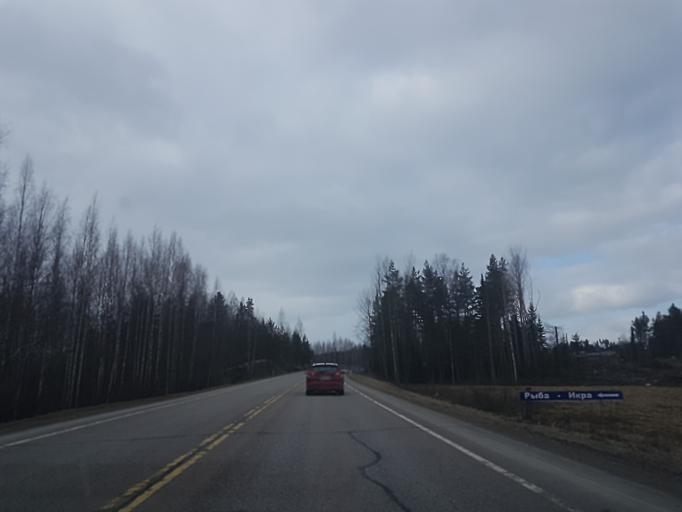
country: FI
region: South Karelia
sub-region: Imatra
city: Parikkala
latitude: 61.4907
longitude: 29.4839
